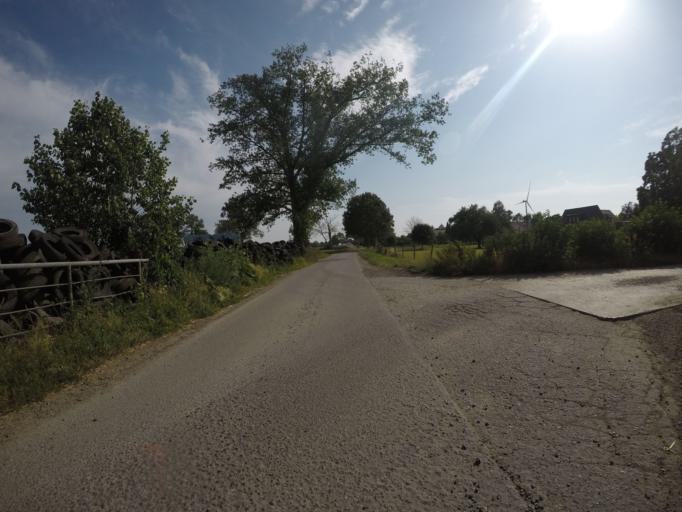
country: DE
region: North Rhine-Westphalia
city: Kalkar
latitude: 51.7460
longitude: 6.3361
